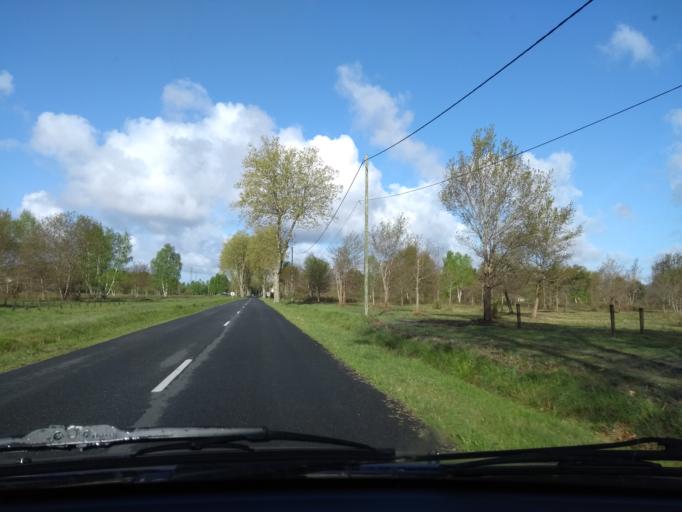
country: FR
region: Aquitaine
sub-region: Departement de la Gironde
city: Mios
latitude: 44.5497
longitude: -0.9864
